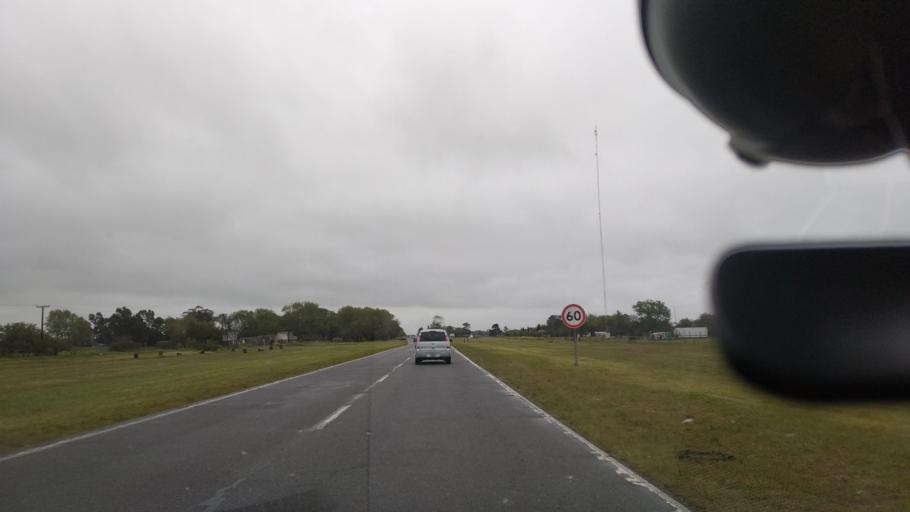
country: AR
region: Buenos Aires
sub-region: Partido de Castelli
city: Castelli
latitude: -35.9804
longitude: -57.4496
